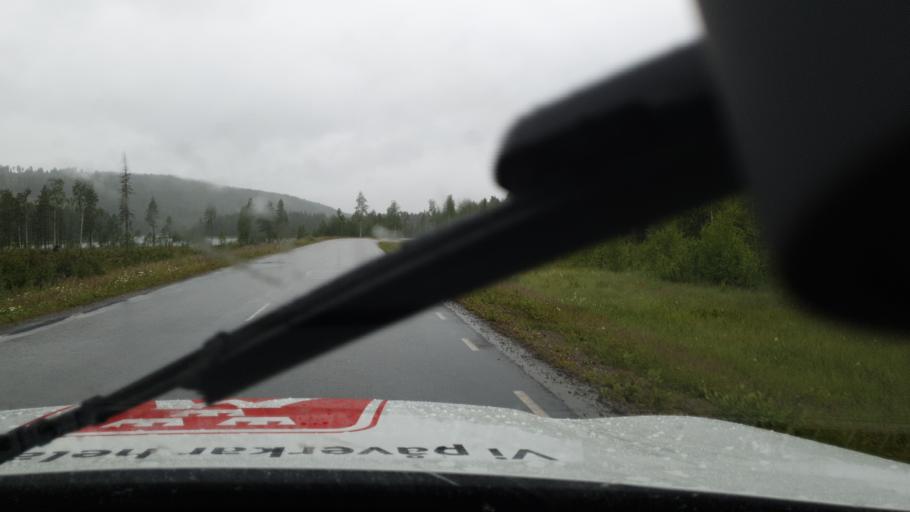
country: SE
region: Vaesterbotten
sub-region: Skelleftea Kommun
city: Langsele
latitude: 64.8219
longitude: 19.9357
